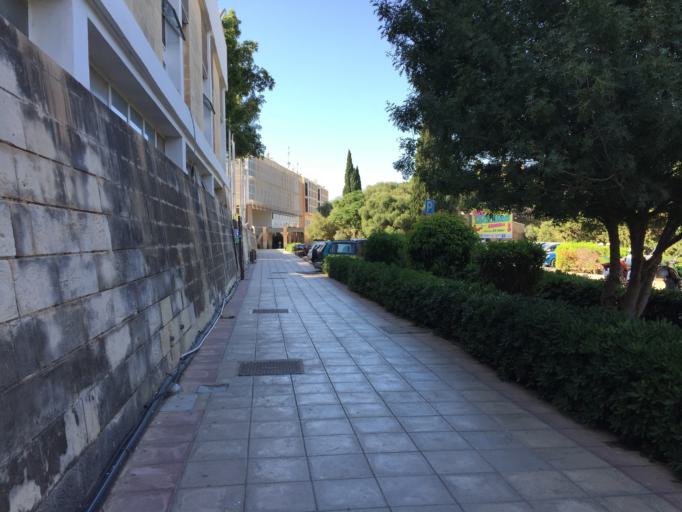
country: MT
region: Il-Gzira
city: Gzira
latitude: 35.9016
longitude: 14.4836
